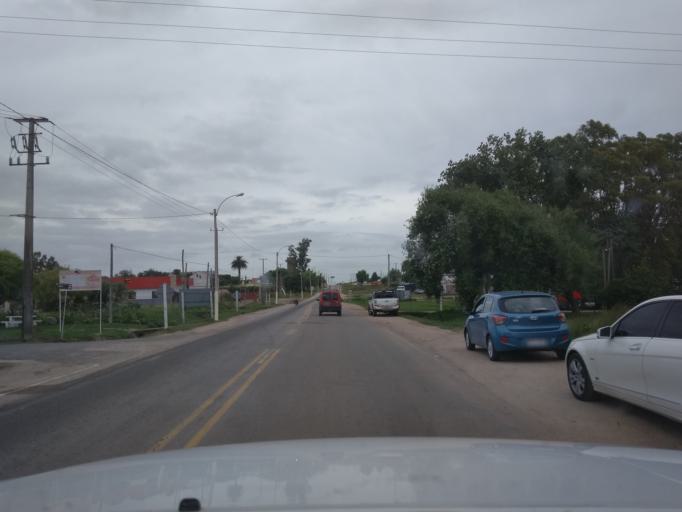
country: UY
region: Canelones
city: Tala
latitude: -34.3474
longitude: -55.7660
